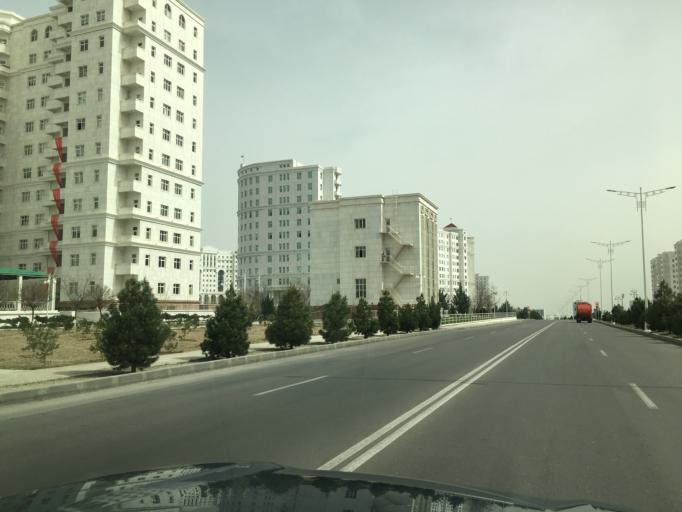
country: TM
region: Ahal
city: Ashgabat
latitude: 37.9192
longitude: 58.3587
